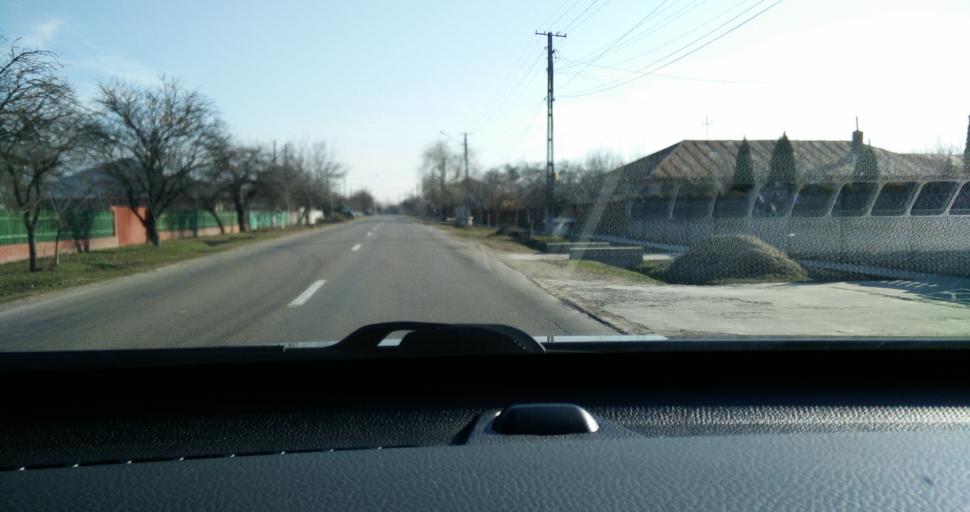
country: RO
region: Vrancea
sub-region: Comuna Nanesti
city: Nanesti
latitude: 45.5401
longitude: 27.4971
